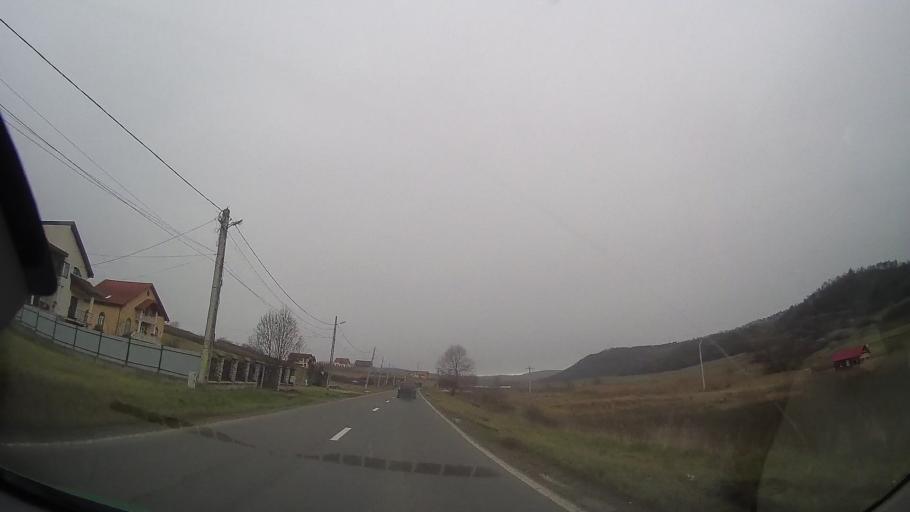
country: RO
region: Mures
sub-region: Comuna Ceausu de Campie
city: Ceausu de Campie
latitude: 46.6227
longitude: 24.5228
